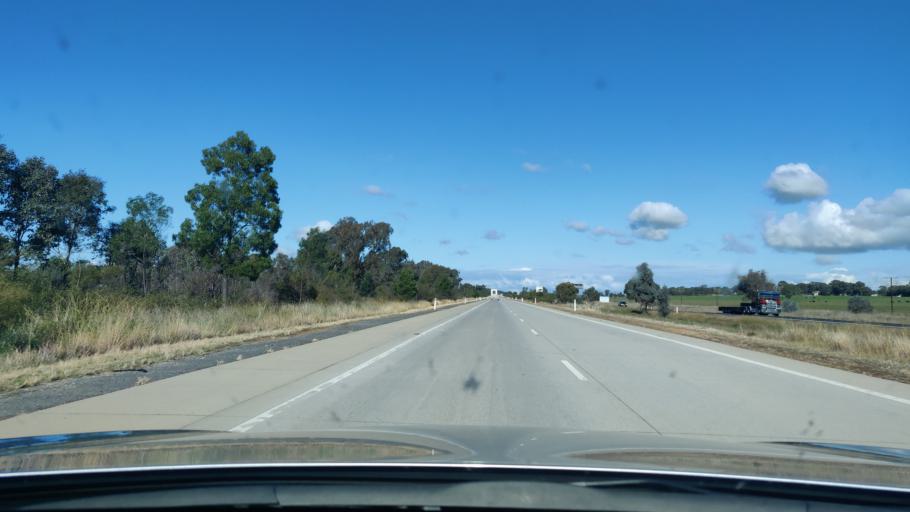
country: AU
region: New South Wales
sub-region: Greater Hume Shire
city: Jindera
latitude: -35.9425
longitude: 147.0036
